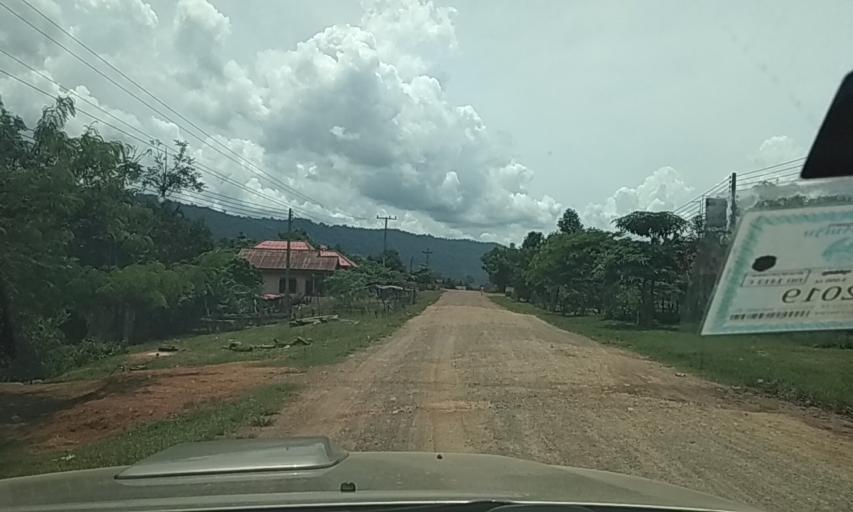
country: LA
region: Bolikhamxai
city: Ban Nahin
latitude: 18.1404
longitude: 104.7588
